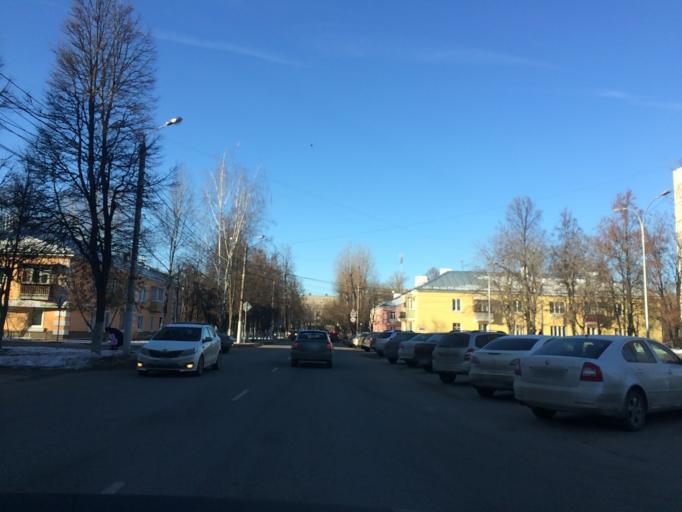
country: RU
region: Tula
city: Mendeleyevskiy
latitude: 54.1709
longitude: 37.5779
